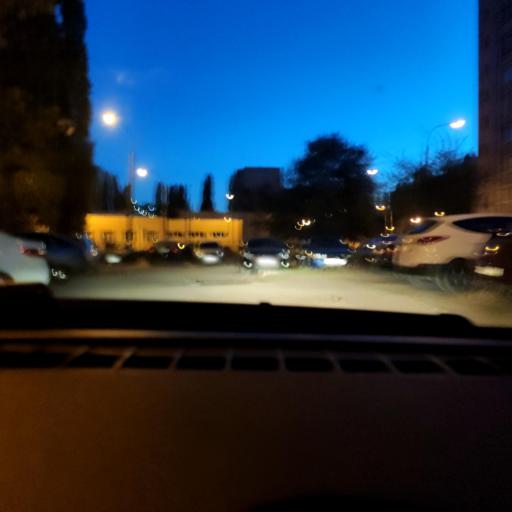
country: RU
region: Voronezj
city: Voronezh
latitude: 51.6424
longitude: 39.2741
